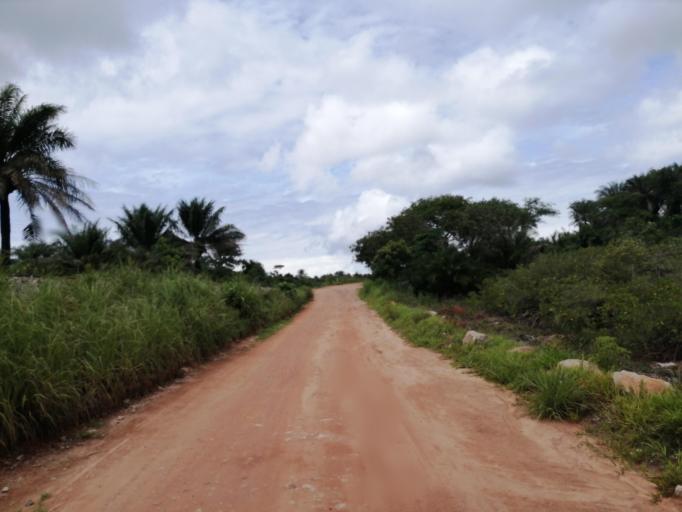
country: SL
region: Northern Province
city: Pepel
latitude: 8.6031
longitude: -13.0525
